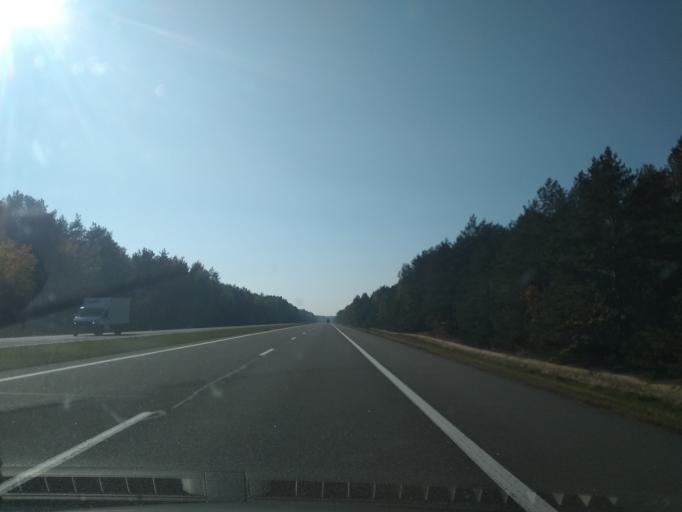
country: BY
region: Brest
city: Antopal'
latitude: 52.3792
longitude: 24.7574
